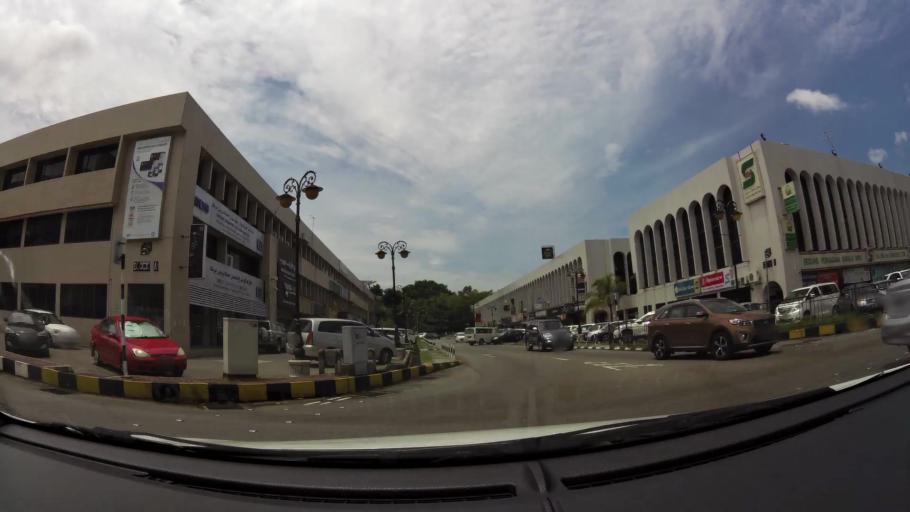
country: BN
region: Brunei and Muara
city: Bandar Seri Begawan
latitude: 4.9068
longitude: 114.9166
